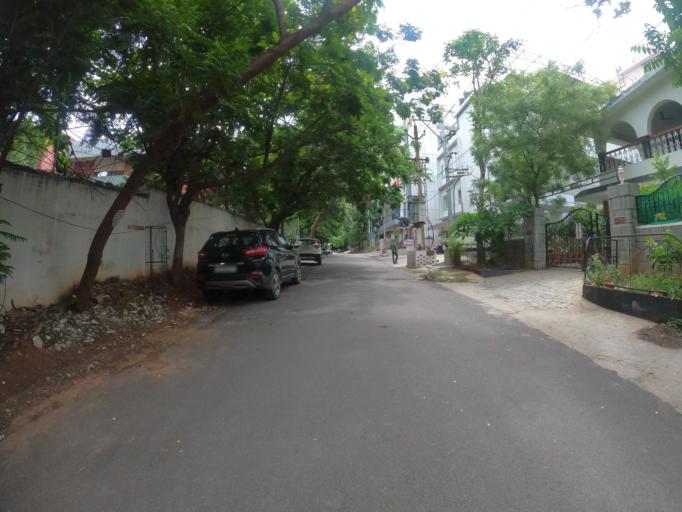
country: IN
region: Telangana
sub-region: Hyderabad
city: Hyderabad
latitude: 17.4271
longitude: 78.4483
